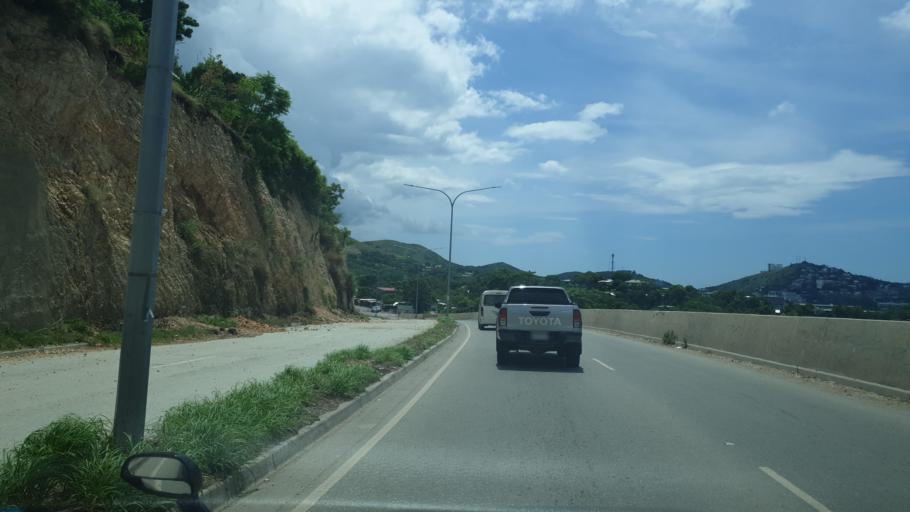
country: PG
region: National Capital
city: Port Moresby
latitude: -9.4487
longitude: 147.1484
